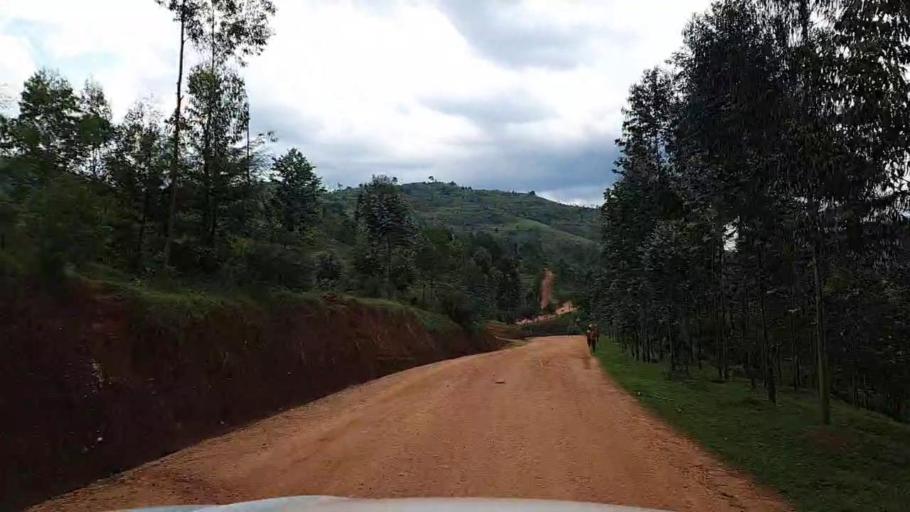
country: RW
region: Southern Province
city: Nyanza
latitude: -2.4018
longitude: 29.6771
